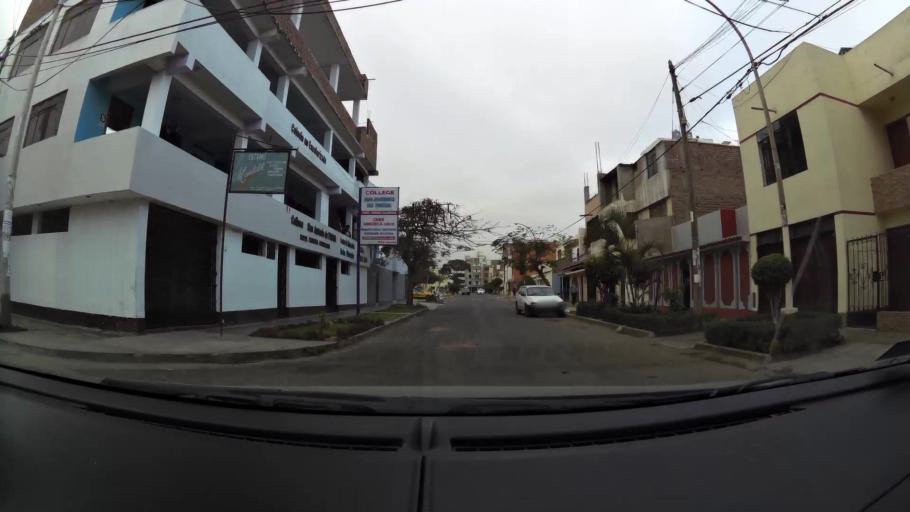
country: PE
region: La Libertad
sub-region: Provincia de Trujillo
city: Trujillo
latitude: -8.0983
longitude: -79.0273
